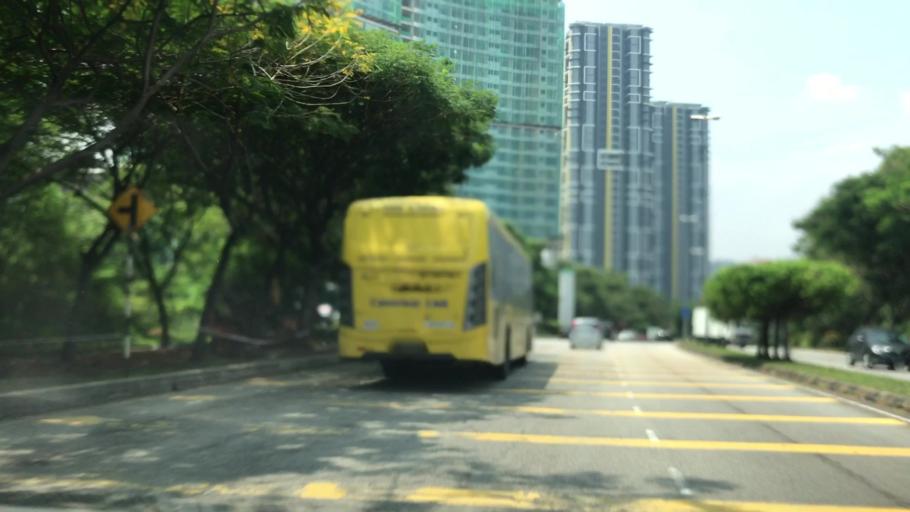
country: MY
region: Selangor
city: Subang Jaya
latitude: 3.0240
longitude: 101.6213
